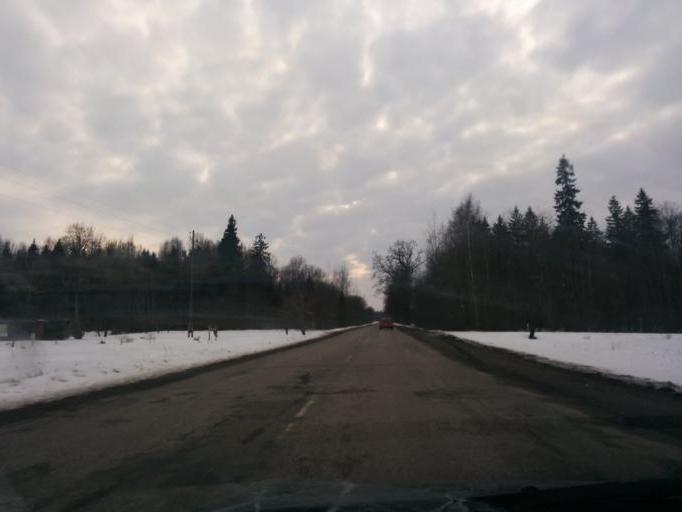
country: LV
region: Gulbenes Rajons
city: Gulbene
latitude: 57.1760
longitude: 26.8148
